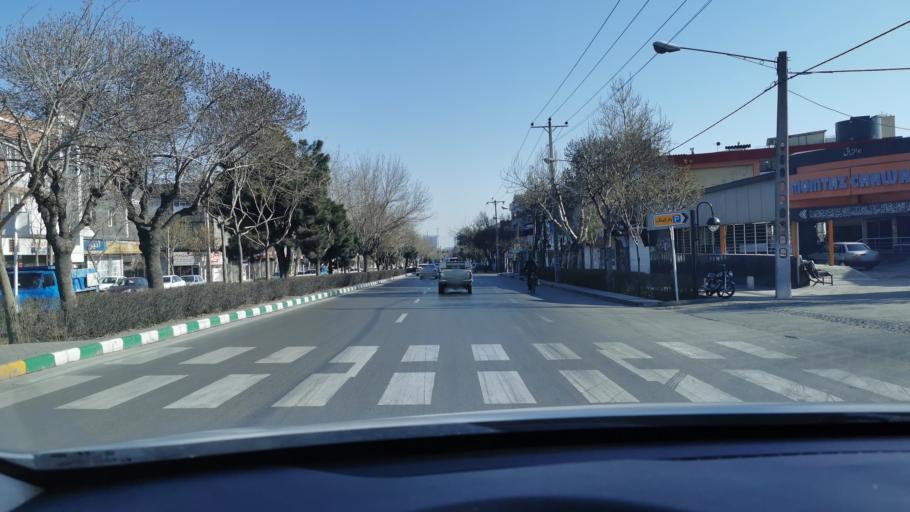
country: IR
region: Razavi Khorasan
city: Mashhad
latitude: 36.2652
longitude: 59.5860
